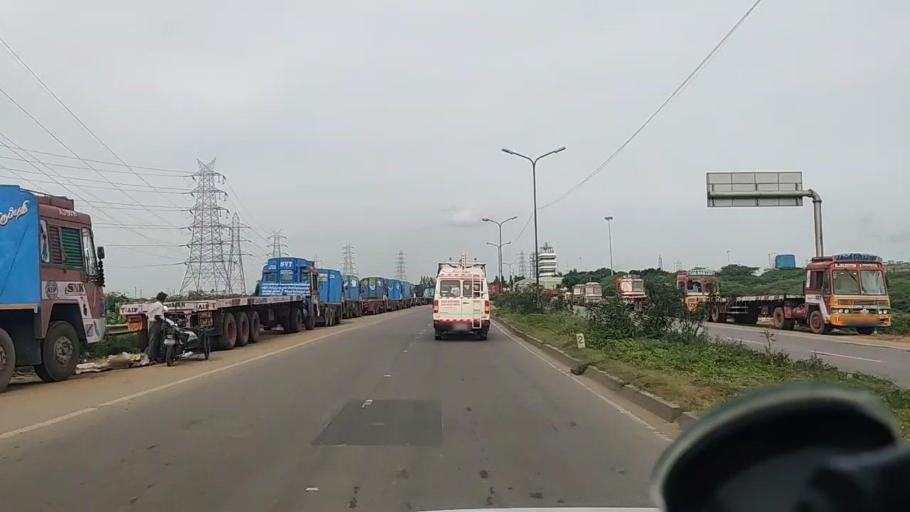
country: IN
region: Tamil Nadu
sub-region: Thiruvallur
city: Manali
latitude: 13.1797
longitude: 80.2533
